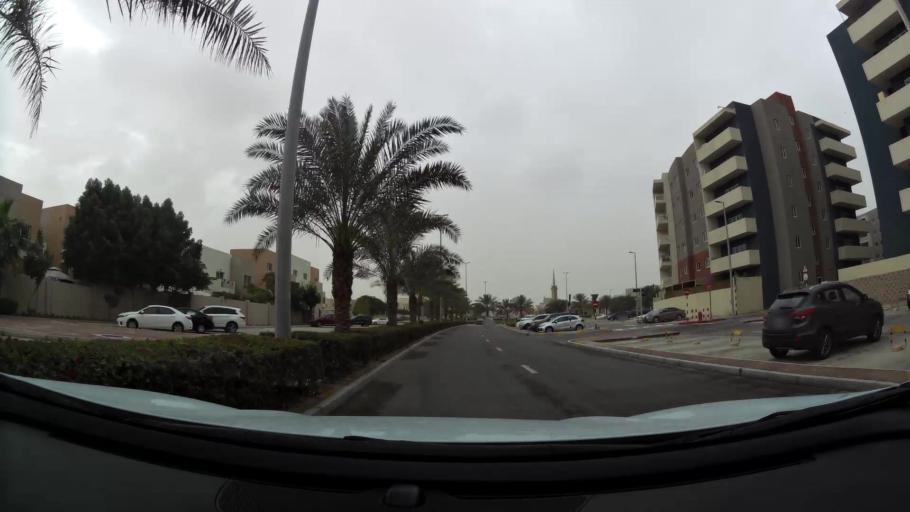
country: AE
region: Abu Dhabi
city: Abu Dhabi
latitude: 24.4553
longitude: 54.6746
